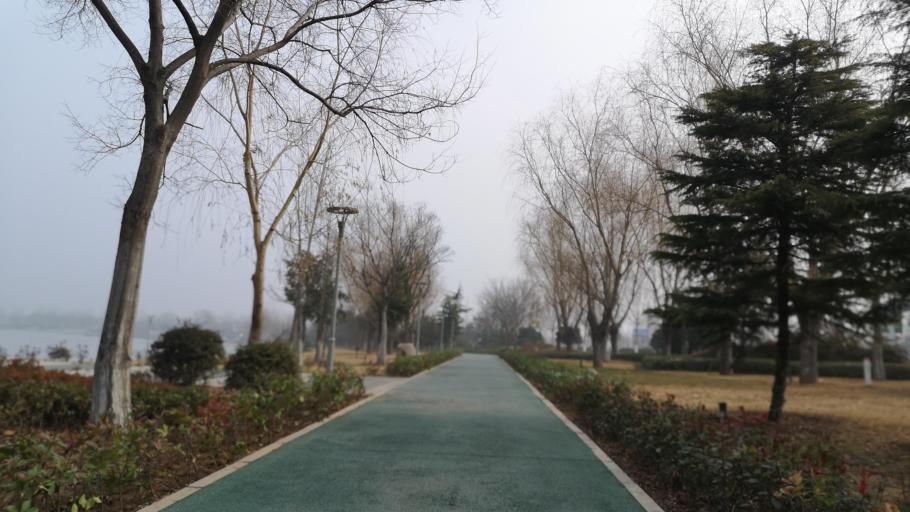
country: CN
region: Henan Sheng
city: Zhongyuanlu
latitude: 35.8001
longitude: 115.0532
